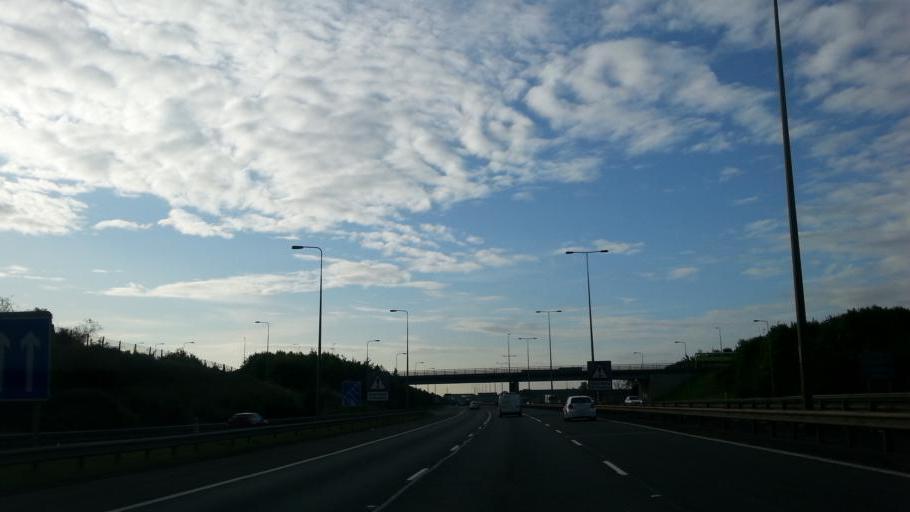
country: GB
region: England
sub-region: Cambridgeshire
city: Stilton
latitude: 52.4999
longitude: -0.2922
